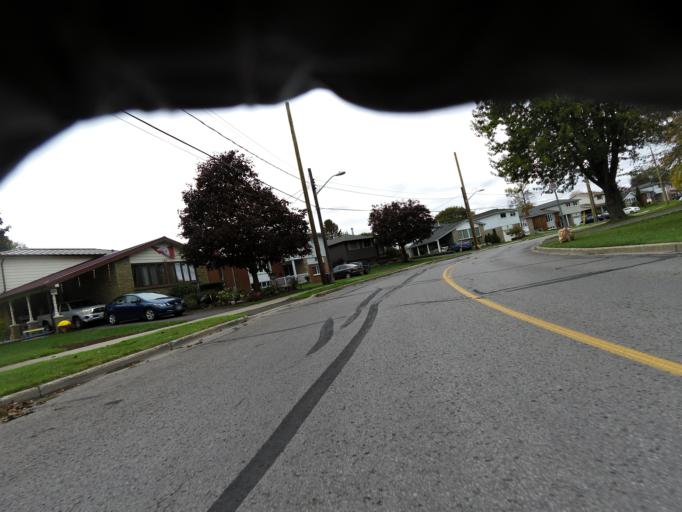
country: CA
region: Ontario
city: Cobourg
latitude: 43.9593
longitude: -78.1914
